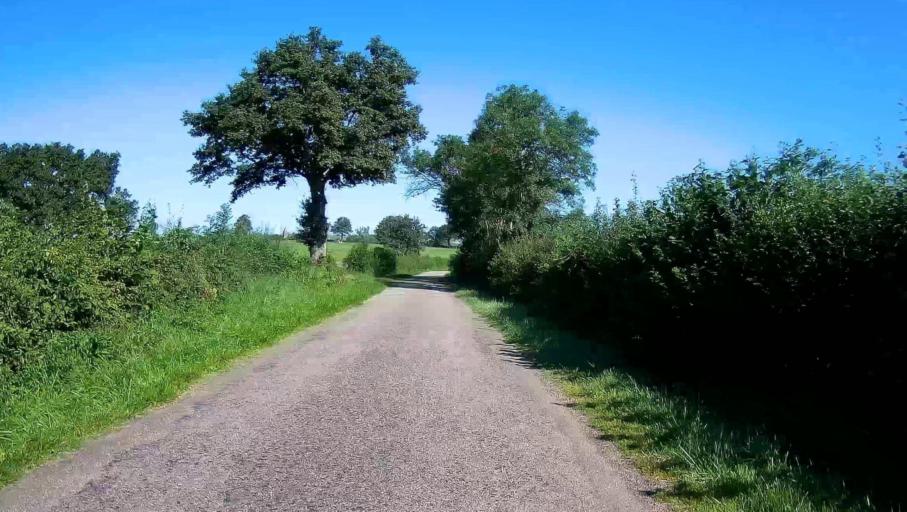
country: FR
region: Bourgogne
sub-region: Departement de Saone-et-Loire
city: Saint-Leger-sur-Dheune
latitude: 46.8301
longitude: 4.5936
